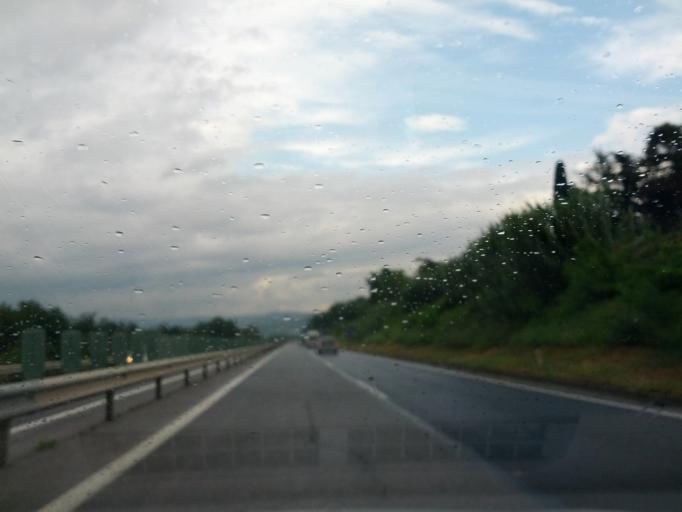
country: SI
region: Koper-Capodistria
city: Koper
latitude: 45.5407
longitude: 13.7482
